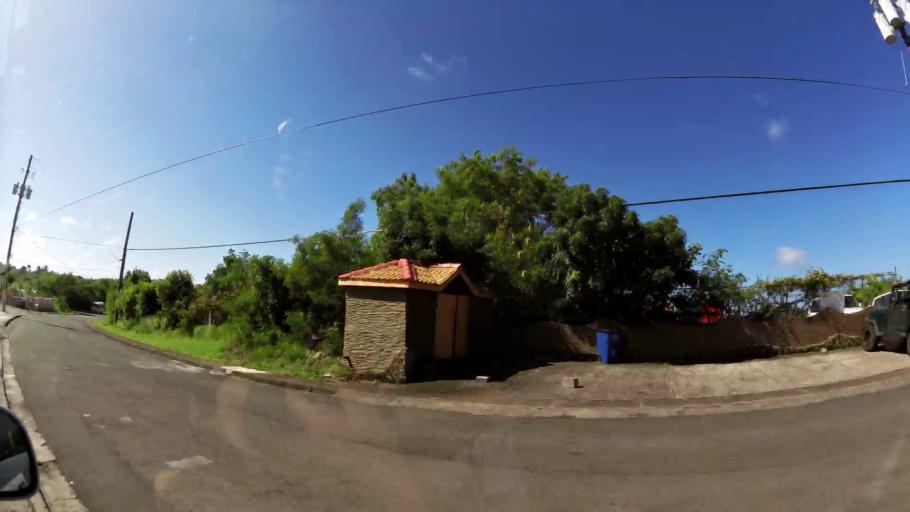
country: GD
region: Saint George
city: Saint George's
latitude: 12.0006
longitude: -61.7678
